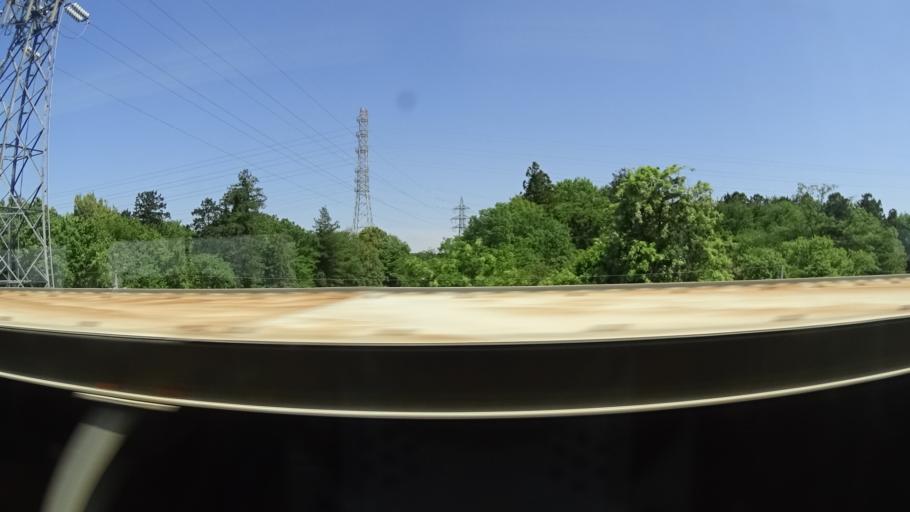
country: JP
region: Tochigi
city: Oyama
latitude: 36.2803
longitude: 139.7803
